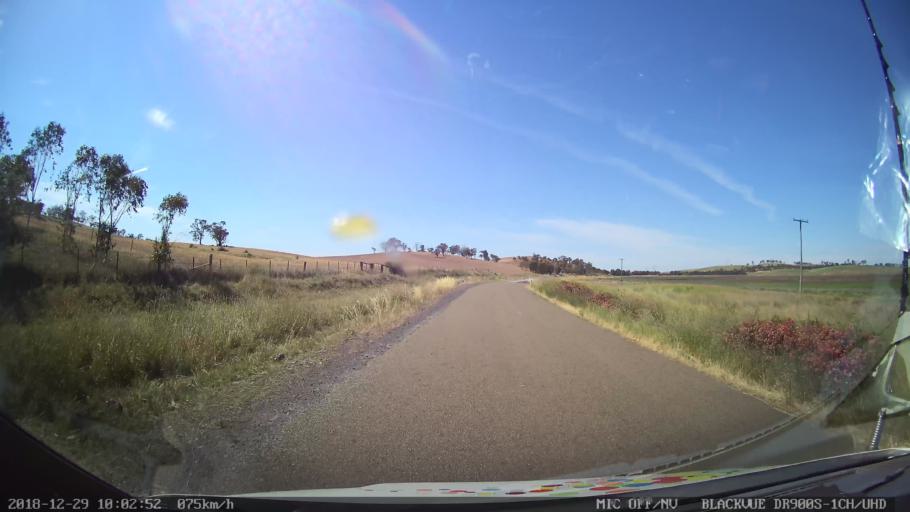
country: AU
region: New South Wales
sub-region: Goulburn Mulwaree
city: Goulburn
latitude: -34.8049
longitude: 149.4613
